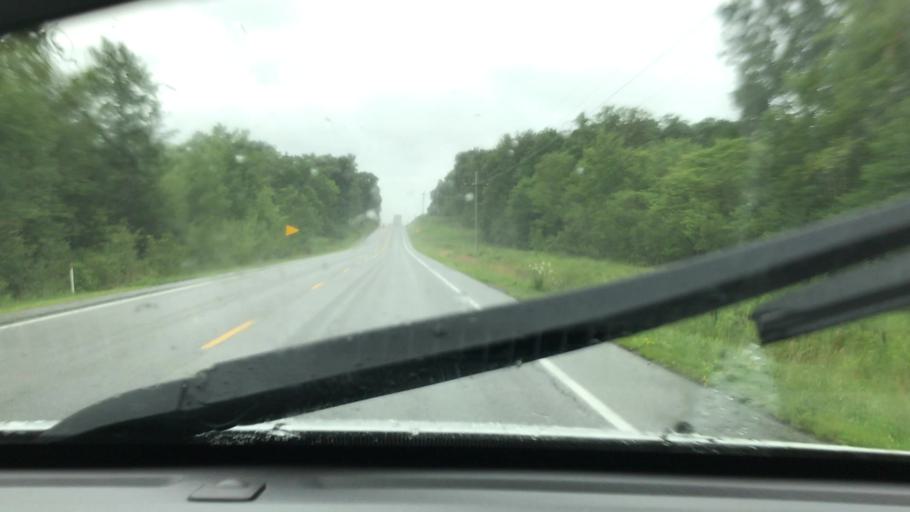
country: US
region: Pennsylvania
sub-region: Centre County
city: Philipsburg
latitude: 40.8476
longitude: -78.2203
